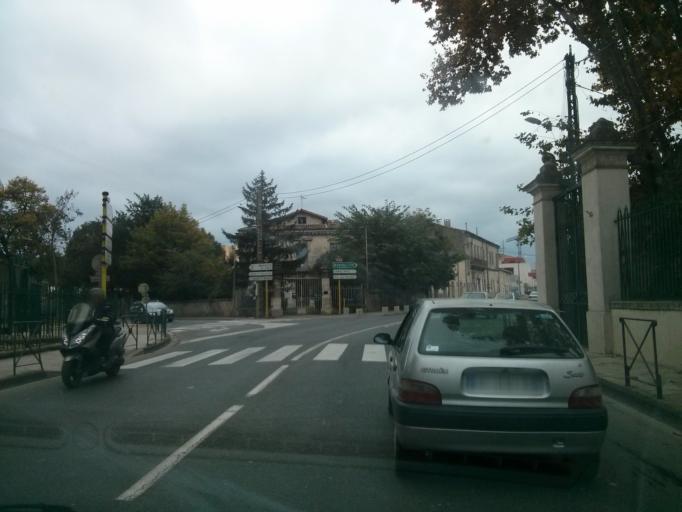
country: FR
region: Languedoc-Roussillon
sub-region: Departement de l'Herault
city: Lunel
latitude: 43.6755
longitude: 4.1304
